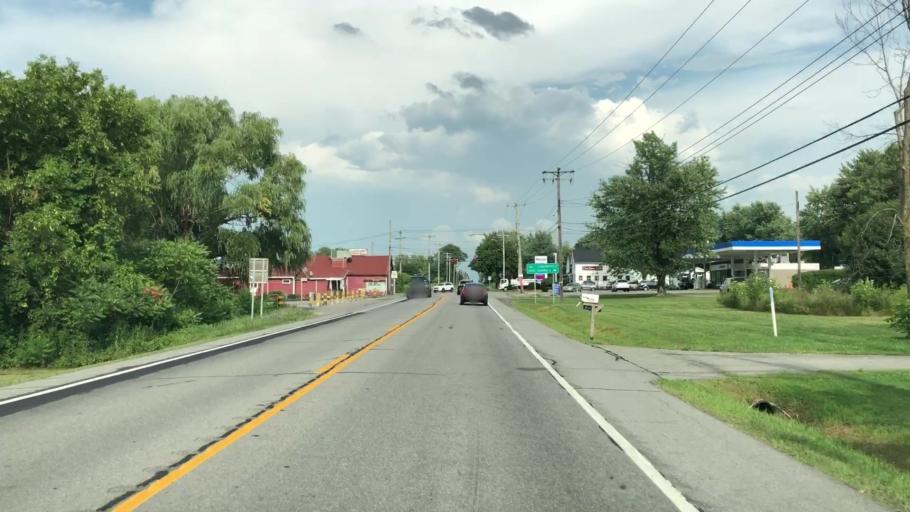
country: US
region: New York
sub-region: Erie County
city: Elma Center
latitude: 42.8556
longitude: -78.6421
